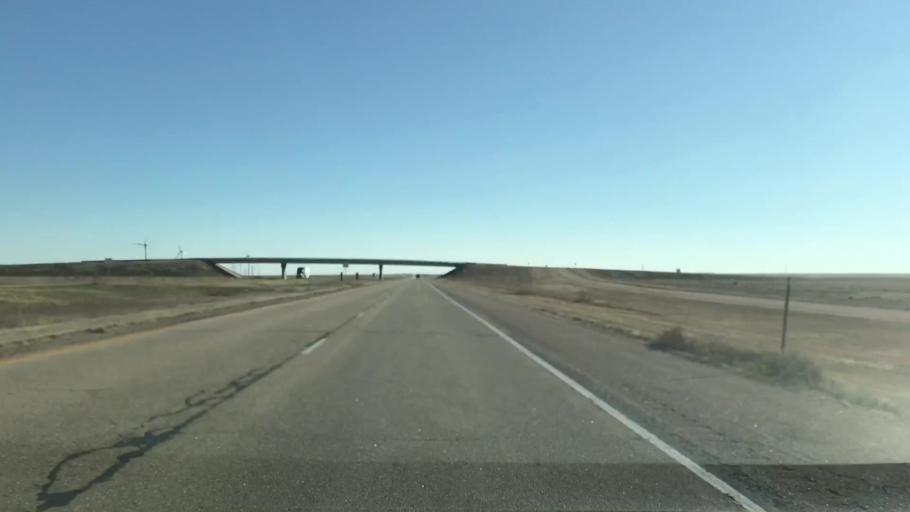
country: US
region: Colorado
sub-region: Lincoln County
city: Hugo
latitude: 39.2775
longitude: -103.4401
